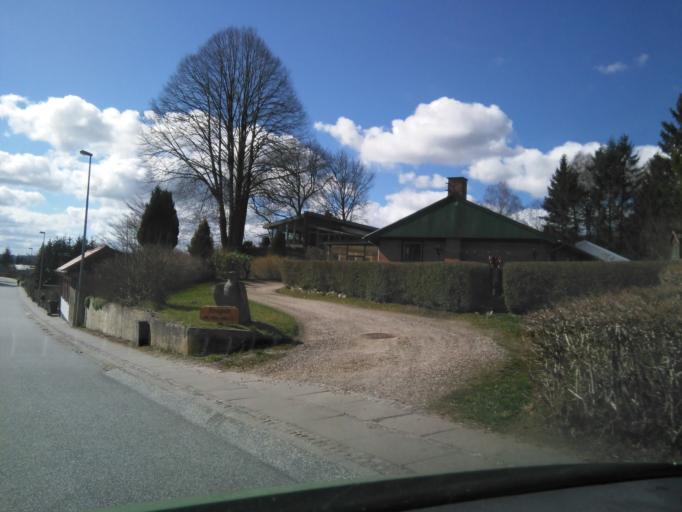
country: DK
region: Central Jutland
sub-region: Skanderborg Kommune
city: Ry
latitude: 56.0736
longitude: 9.6978
